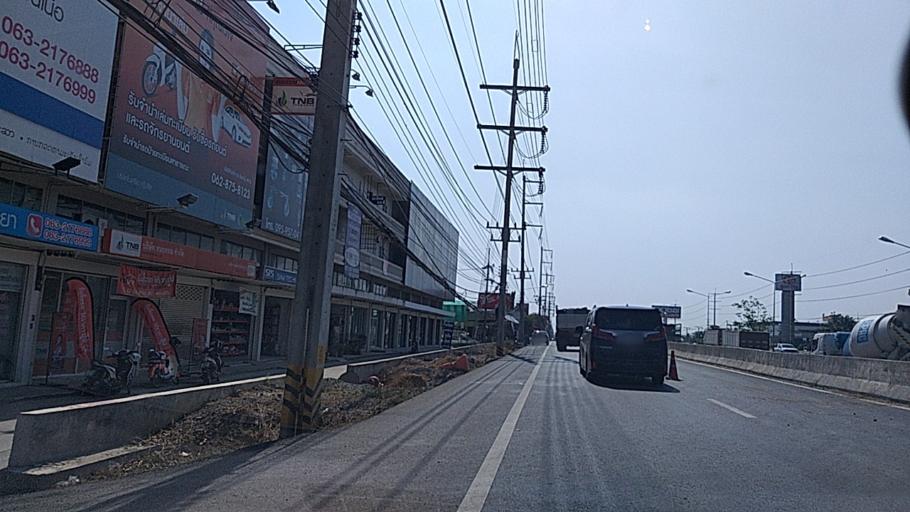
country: TH
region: Nakhon Pathom
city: Salaya
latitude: 13.7852
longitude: 100.2679
